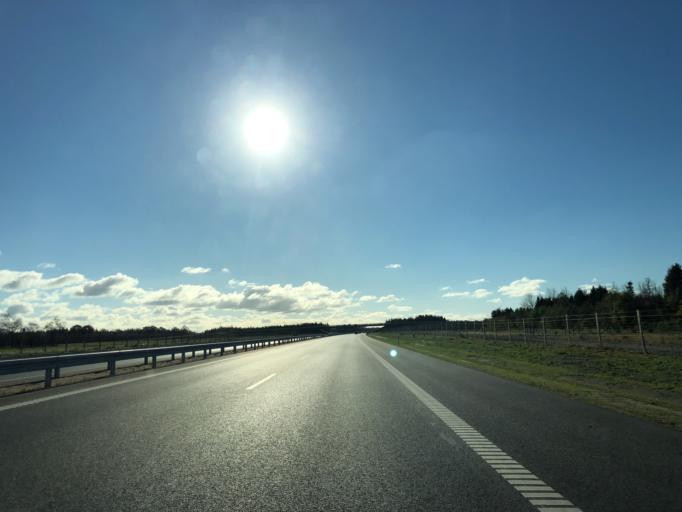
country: DK
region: Central Jutland
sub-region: Herning Kommune
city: Avlum
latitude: 56.3417
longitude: 8.7378
